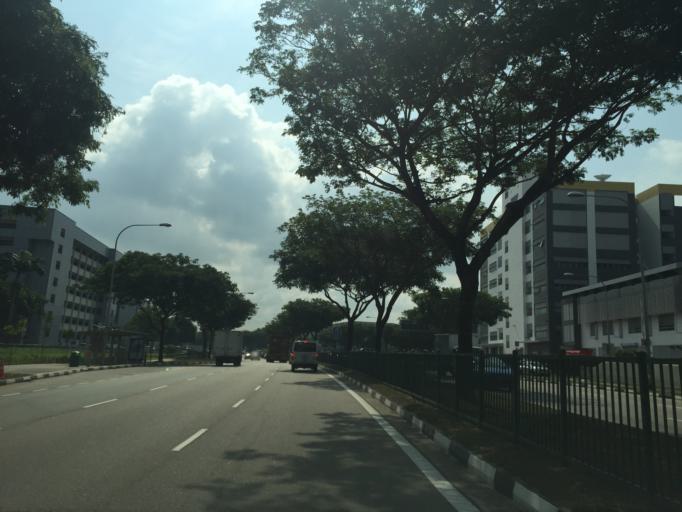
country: SG
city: Singapore
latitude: 1.3347
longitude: 103.8920
